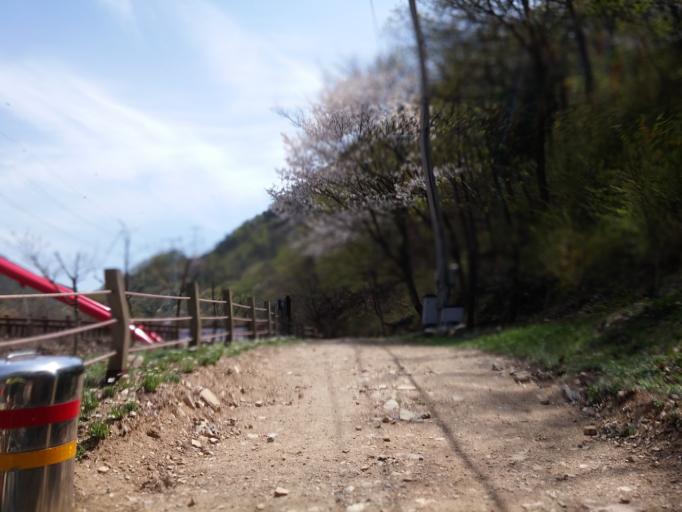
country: KR
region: Chungcheongbuk-do
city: Okcheon
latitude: 36.2399
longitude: 127.5556
